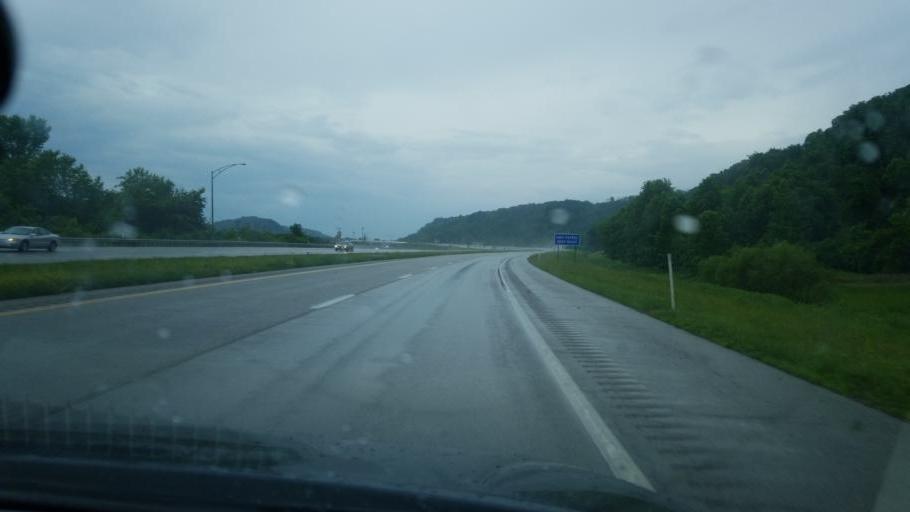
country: US
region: Ohio
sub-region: Athens County
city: Athens
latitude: 39.3345
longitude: -82.0249
